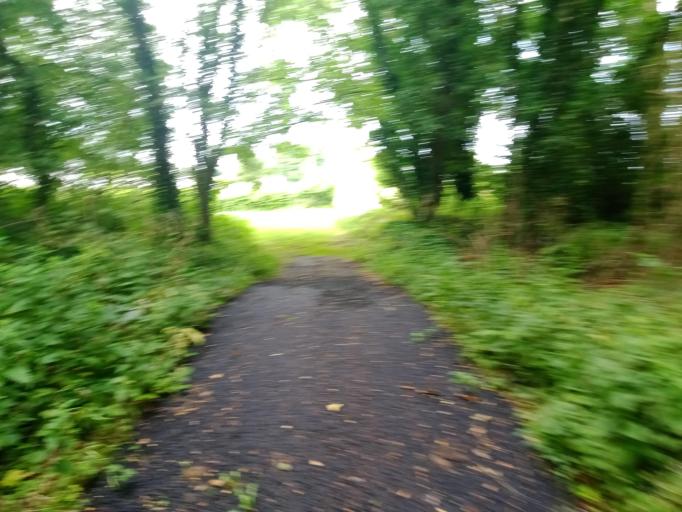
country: IE
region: Leinster
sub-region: Laois
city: Abbeyleix
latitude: 52.8835
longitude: -7.3576
